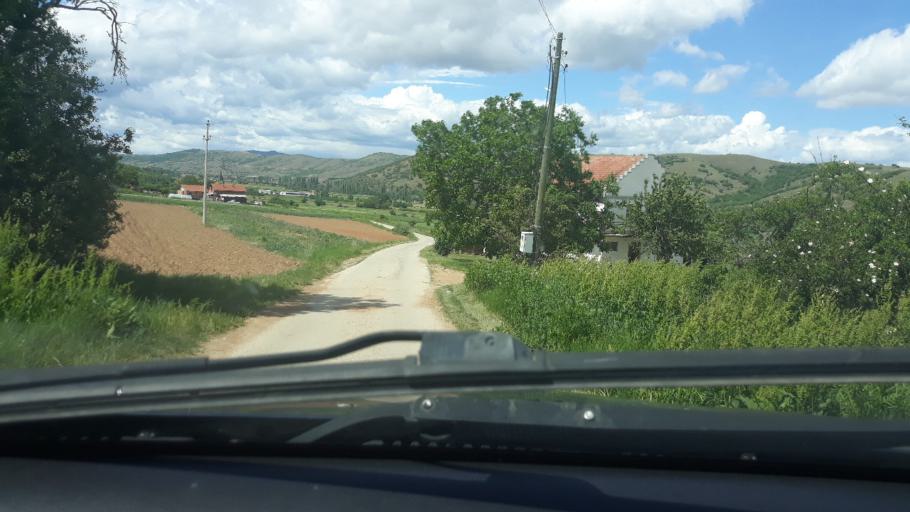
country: MK
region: Krivogastani
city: Krivogashtani
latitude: 41.3374
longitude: 21.3004
